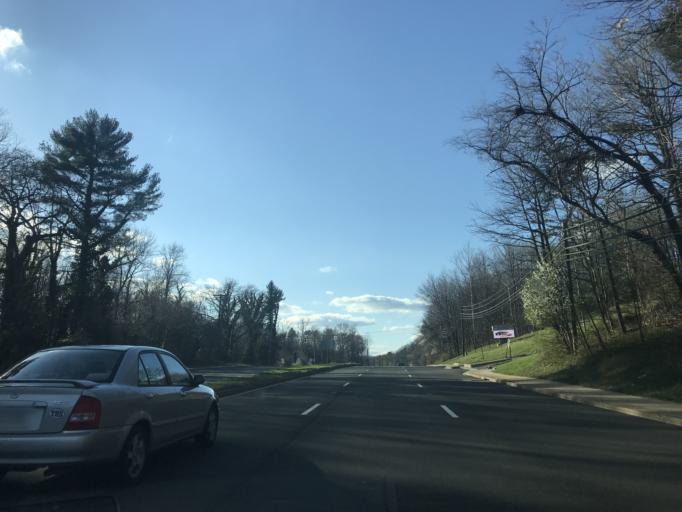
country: US
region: Maryland
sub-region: Prince George's County
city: Glenarden
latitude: 38.9211
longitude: -76.8651
